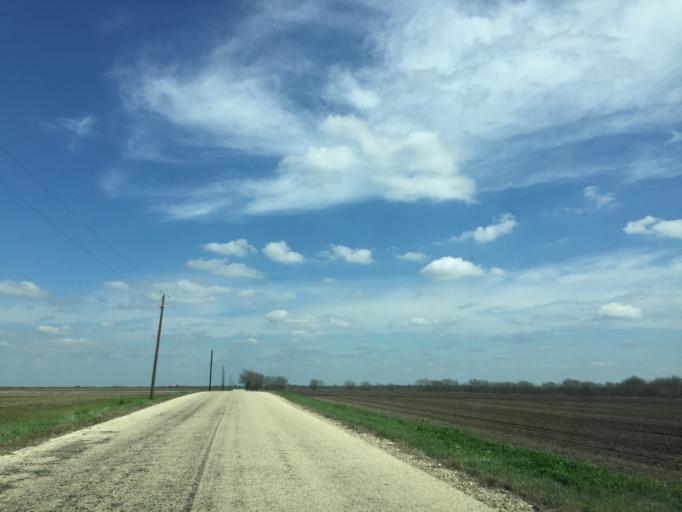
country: US
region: Texas
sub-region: Milam County
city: Thorndale
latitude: 30.5561
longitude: -97.2495
